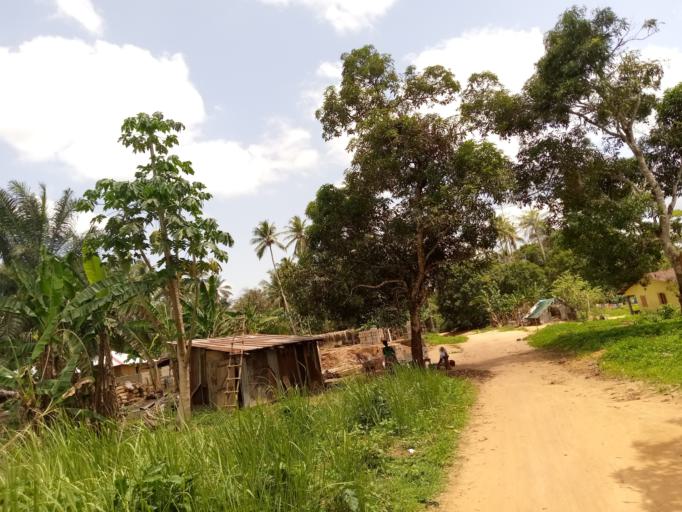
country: SL
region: Western Area
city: Waterloo
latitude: 8.4296
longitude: -13.0129
